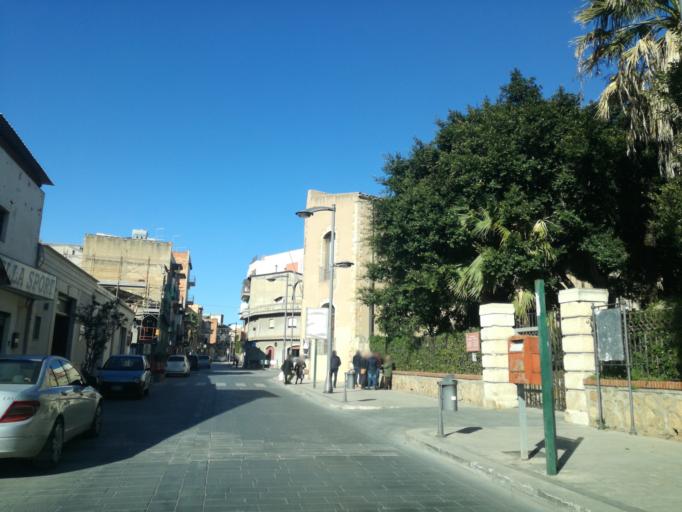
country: IT
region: Sicily
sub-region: Provincia di Caltanissetta
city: Gela
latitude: 37.0713
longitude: 14.2368
